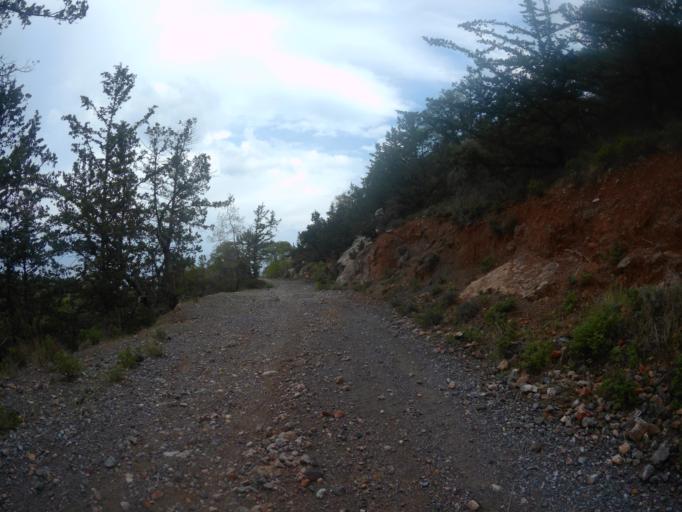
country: CY
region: Ammochostos
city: Lefkonoiko
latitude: 35.3213
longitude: 33.6179
